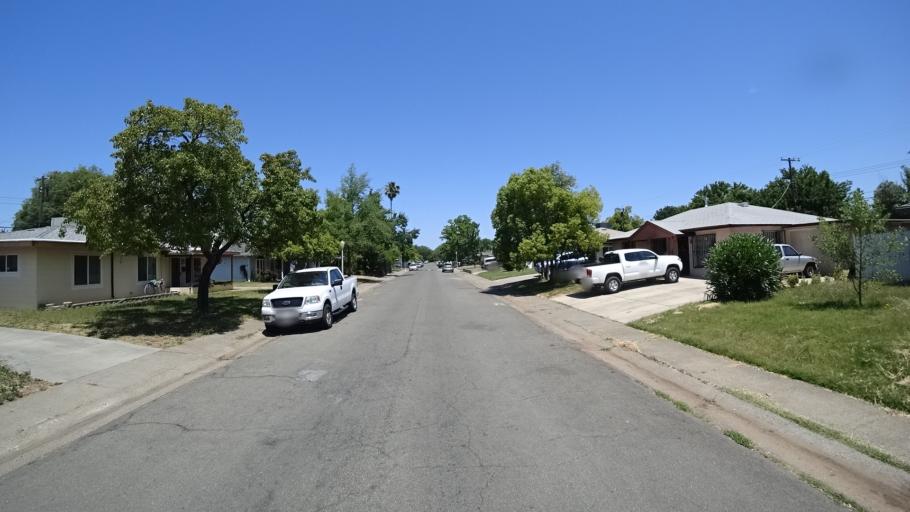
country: US
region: California
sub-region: Sacramento County
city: Parkway
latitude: 38.5263
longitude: -121.4354
